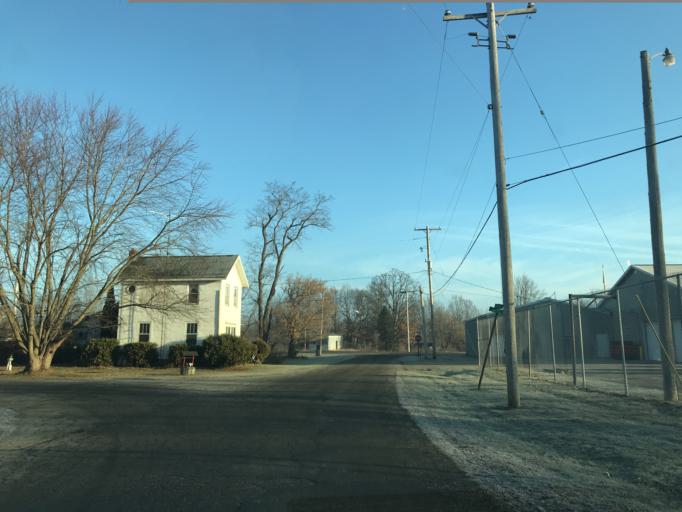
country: US
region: Michigan
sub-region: Eaton County
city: Eaton Rapids
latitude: 42.4441
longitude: -84.5635
